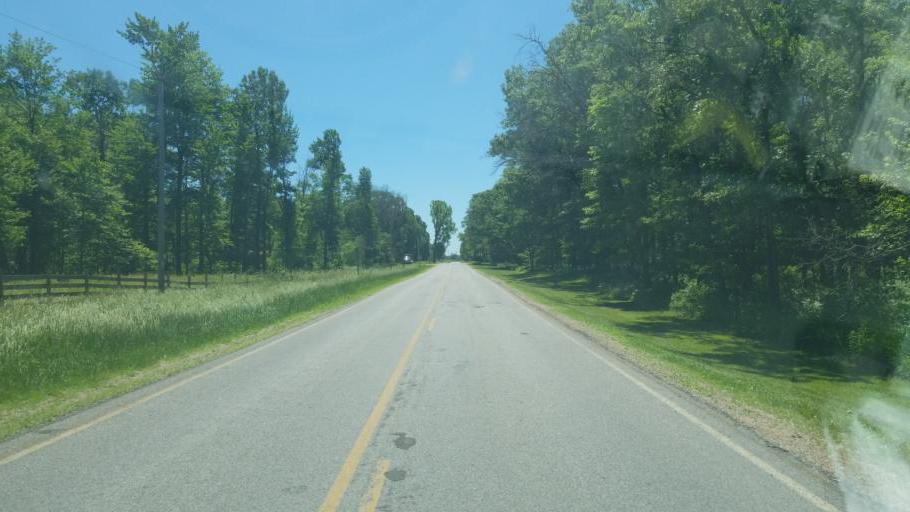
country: US
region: Wisconsin
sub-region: Juneau County
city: New Lisbon
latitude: 44.0241
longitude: -90.2719
